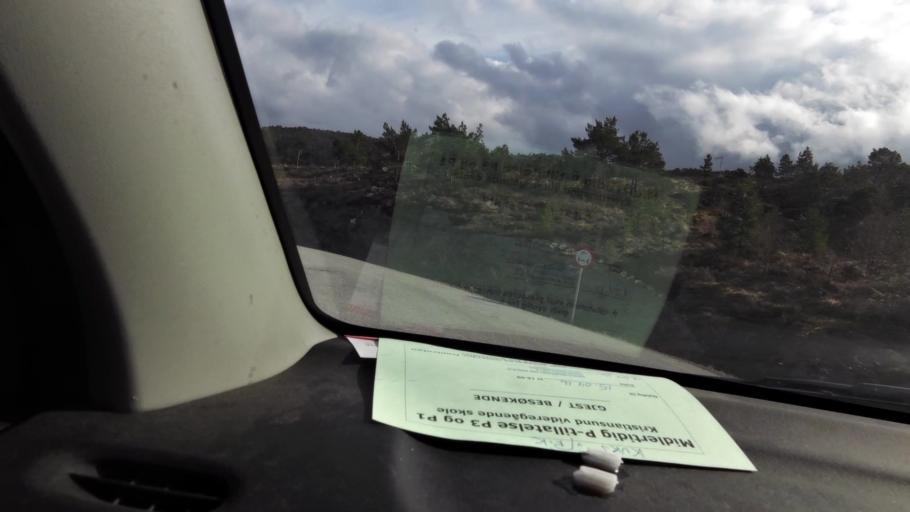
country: NO
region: More og Romsdal
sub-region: Kristiansund
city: Rensvik
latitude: 63.0855
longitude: 7.7865
